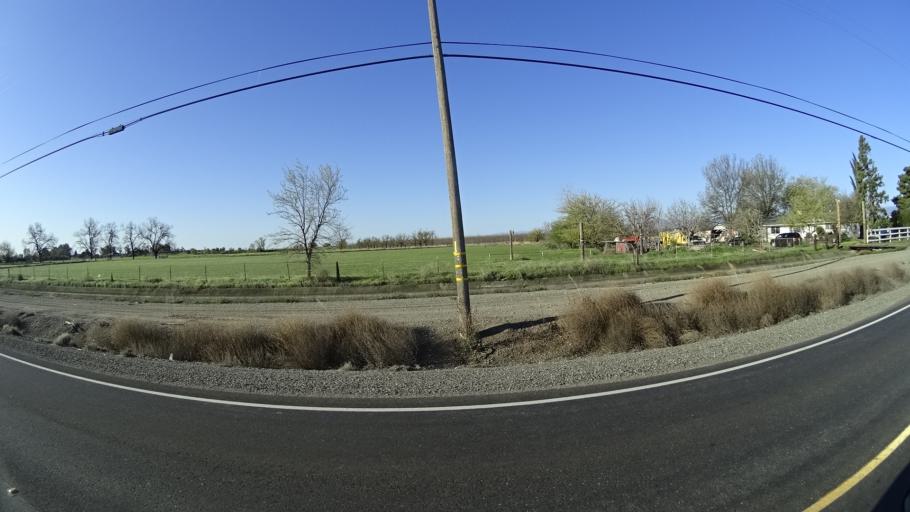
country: US
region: California
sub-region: Glenn County
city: Orland
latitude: 39.7679
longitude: -122.2510
